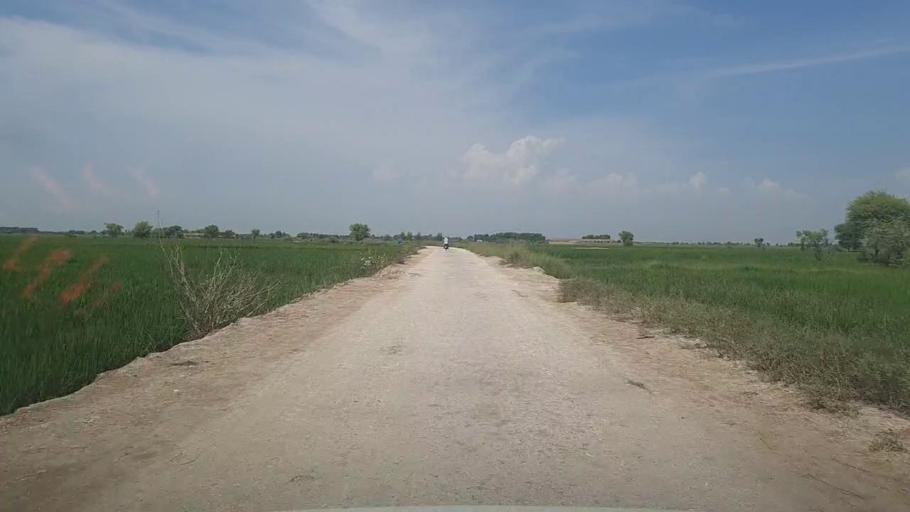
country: PK
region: Sindh
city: Kandhkot
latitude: 28.2835
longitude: 69.2379
